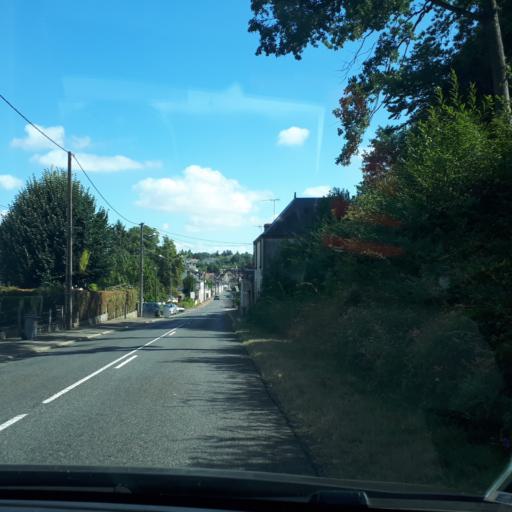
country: FR
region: Centre
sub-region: Departement du Loir-et-Cher
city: Moree
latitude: 47.8984
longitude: 1.2316
